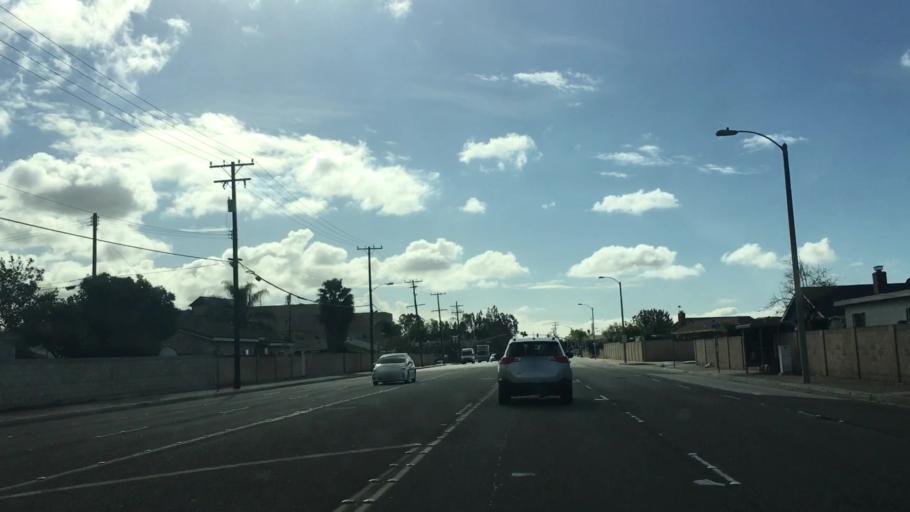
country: US
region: California
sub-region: Orange County
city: Midway City
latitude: 33.7475
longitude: -117.9723
